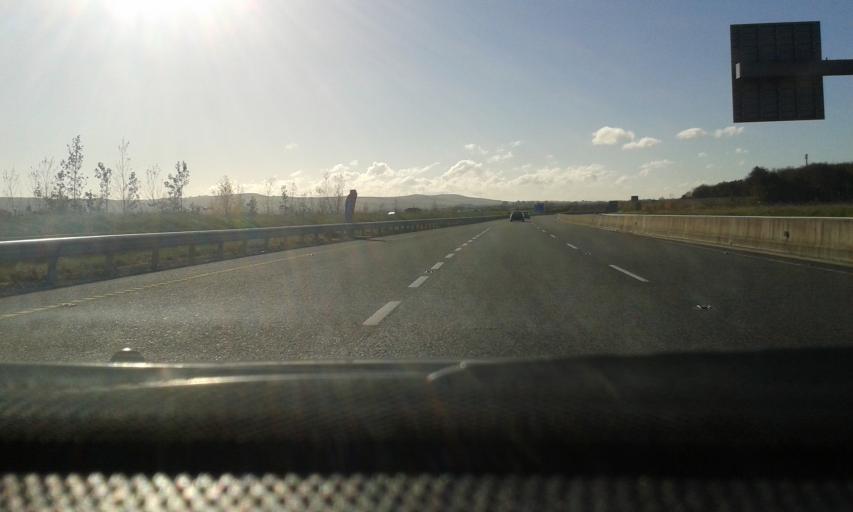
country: IE
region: Leinster
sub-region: Laois
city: Rathdowney
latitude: 52.8603
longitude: -7.4849
